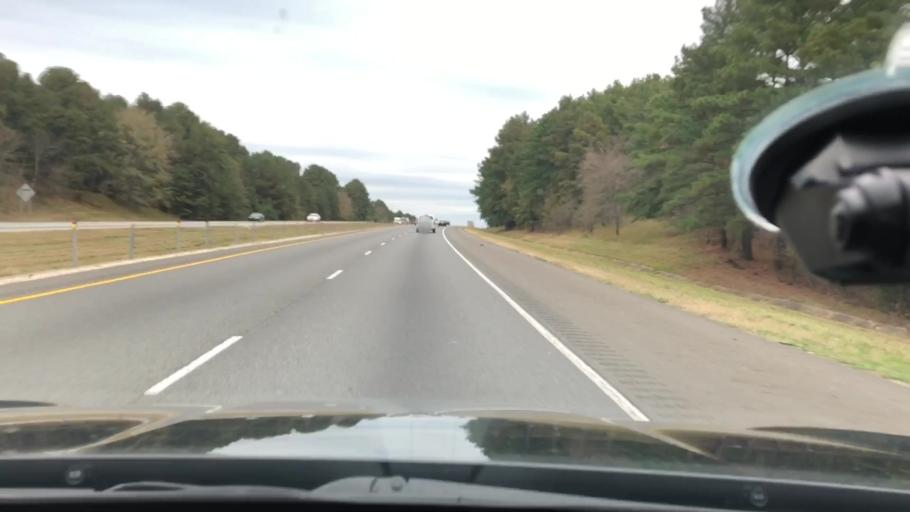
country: US
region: Arkansas
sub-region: Hot Spring County
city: Malvern
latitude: 34.3190
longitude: -92.9332
